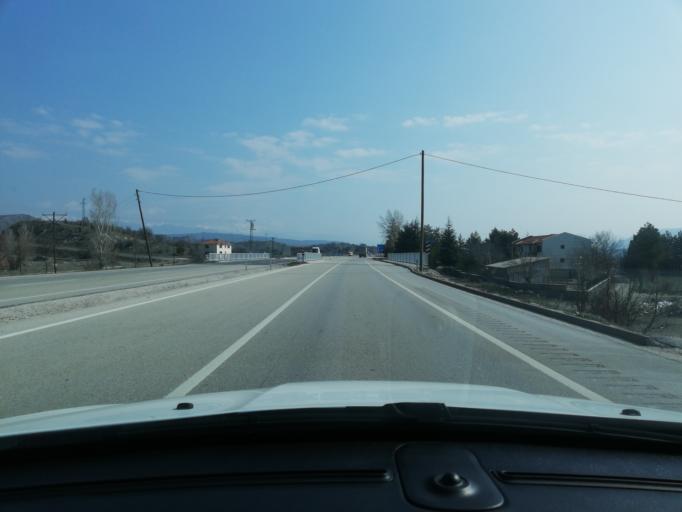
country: TR
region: Cankiri
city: Beloren
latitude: 40.8655
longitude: 33.4849
